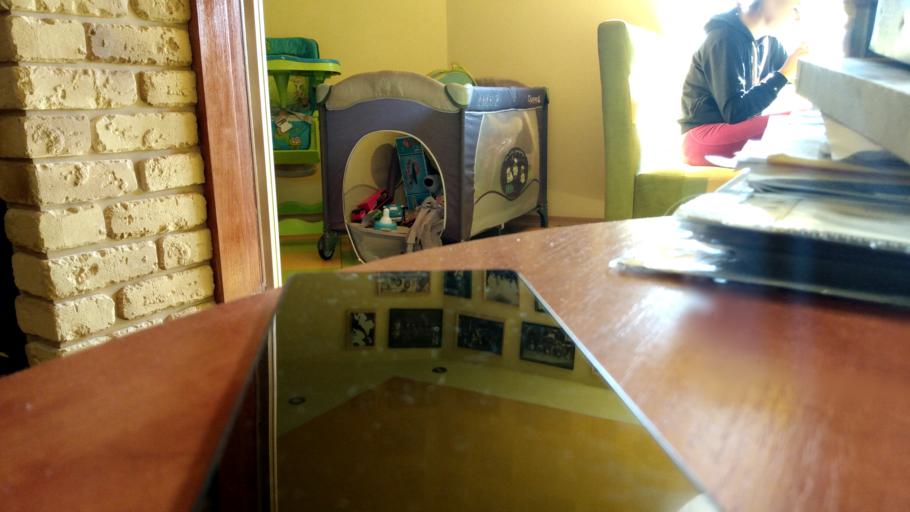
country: RU
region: Penza
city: Serdobsk
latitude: 52.4414
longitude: 44.2984
